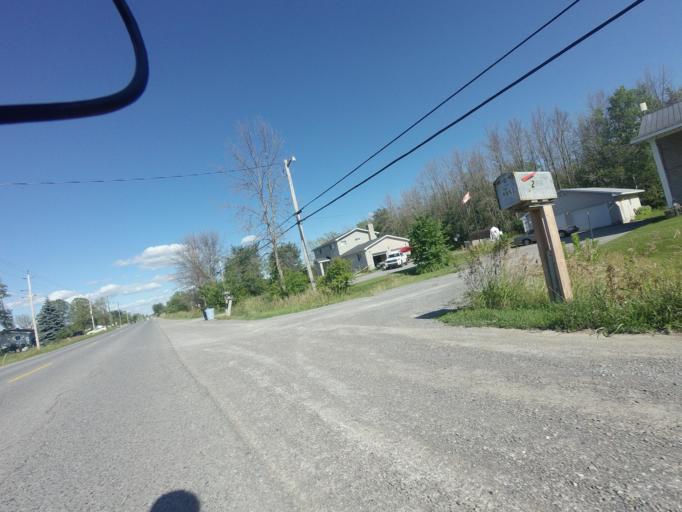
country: CA
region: Ontario
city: Arnprior
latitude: 45.4200
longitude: -76.3917
